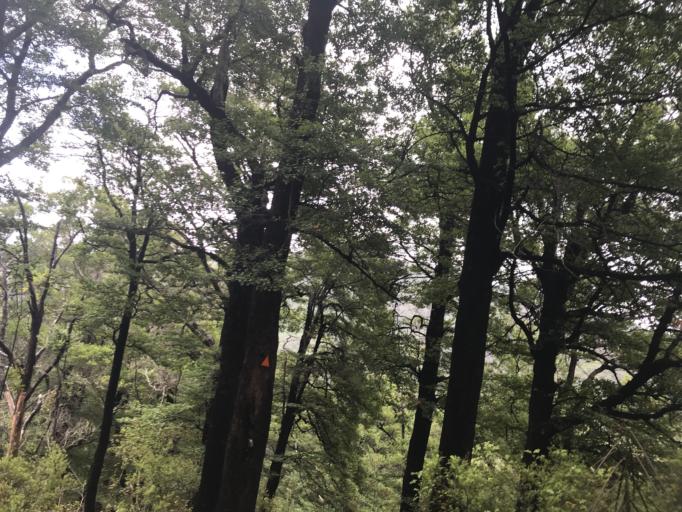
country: NZ
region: Marlborough
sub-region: Marlborough District
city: Picton
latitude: -41.2198
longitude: 173.9751
